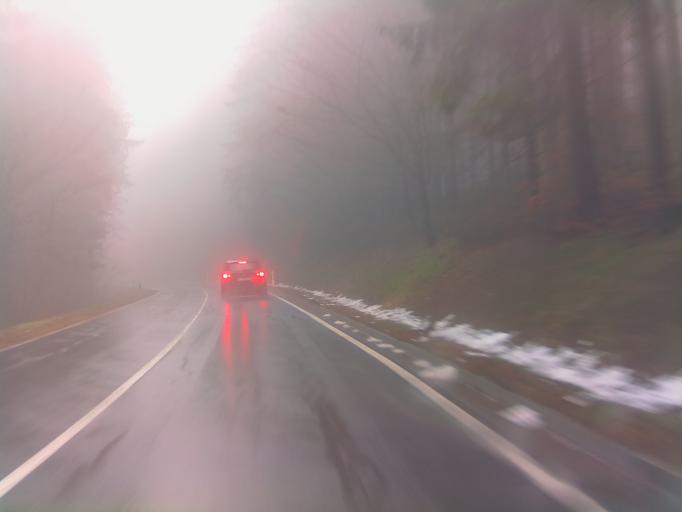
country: DE
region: Thuringia
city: Eisfeld
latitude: 50.4603
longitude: 10.9038
